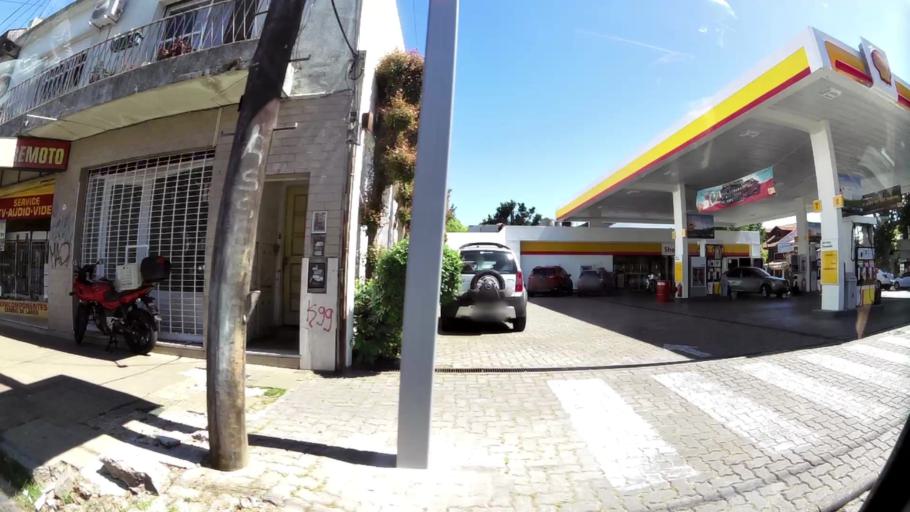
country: AR
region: Buenos Aires
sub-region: Partido de Vicente Lopez
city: Olivos
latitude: -34.5165
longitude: -58.4966
